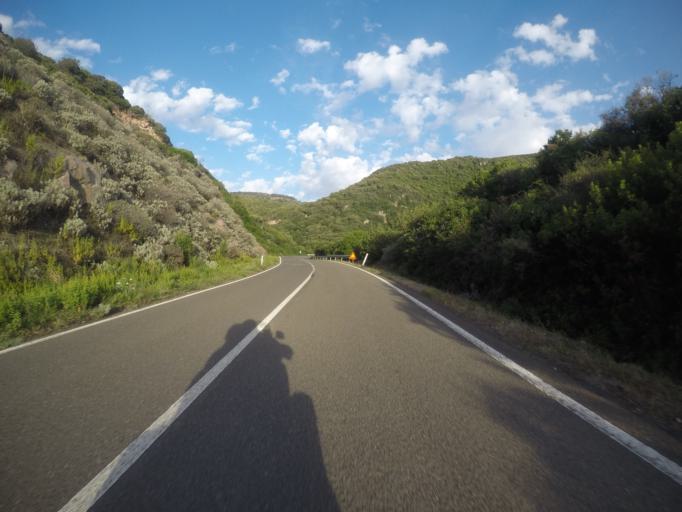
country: IT
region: Sardinia
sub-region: Provincia di Sassari
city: Villanova Monteleone
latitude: 40.4357
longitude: 8.4047
